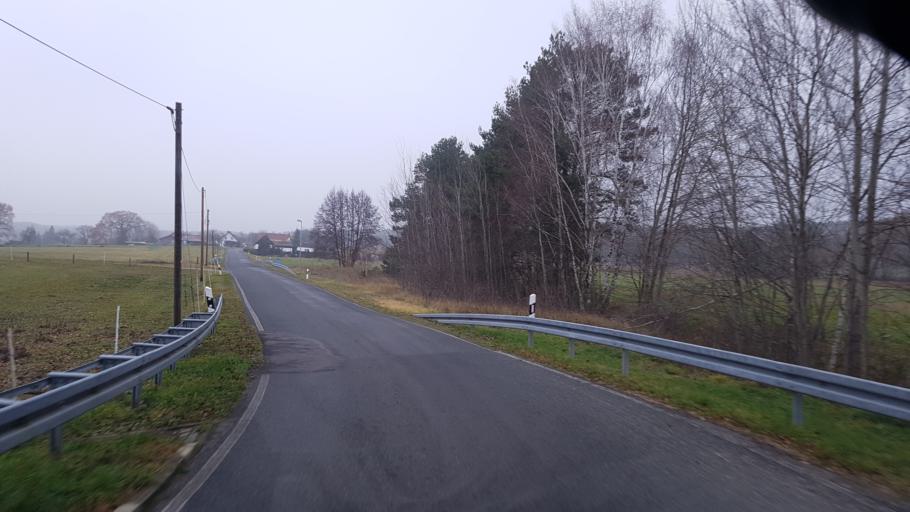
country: DE
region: Brandenburg
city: Calau
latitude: 51.6881
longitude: 13.9752
